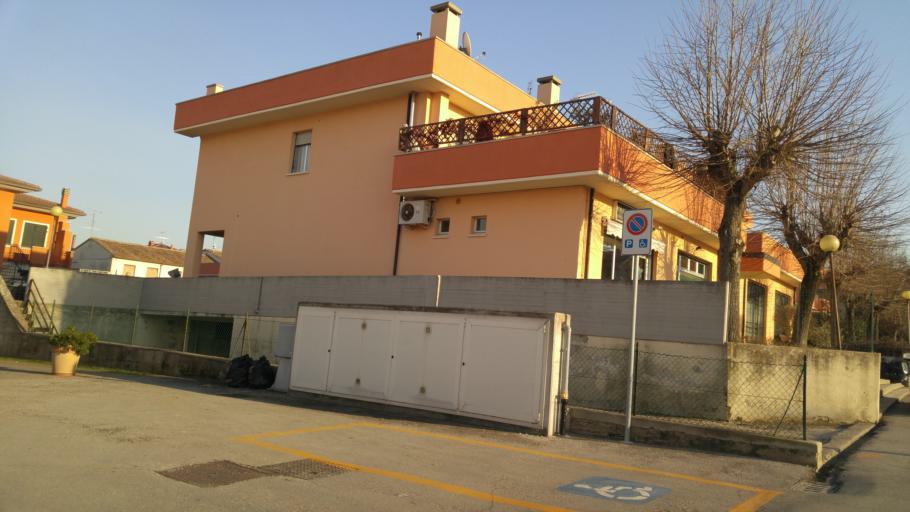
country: IT
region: The Marches
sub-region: Provincia di Pesaro e Urbino
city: Villanova
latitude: 43.7408
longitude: 12.9329
